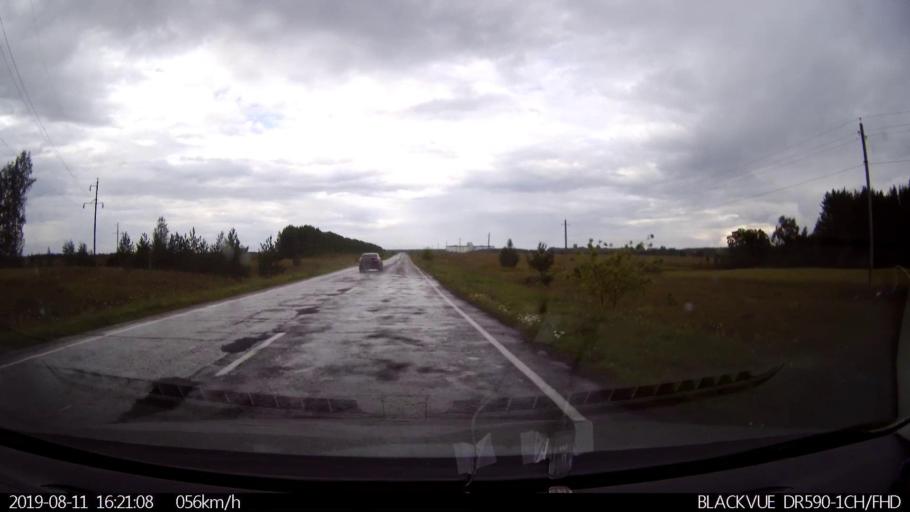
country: RU
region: Ulyanovsk
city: Mayna
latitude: 54.0775
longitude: 47.5994
